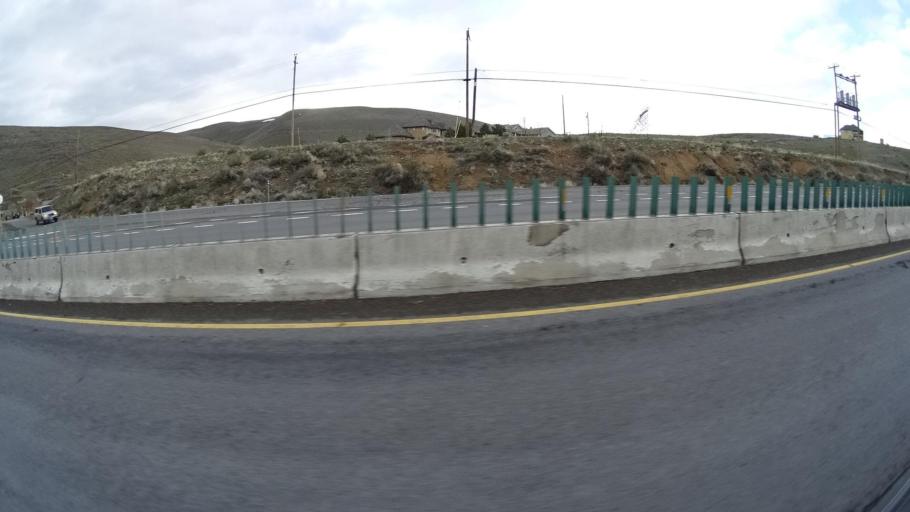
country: US
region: Nevada
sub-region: Storey County
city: Virginia City
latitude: 39.3346
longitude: -119.7825
